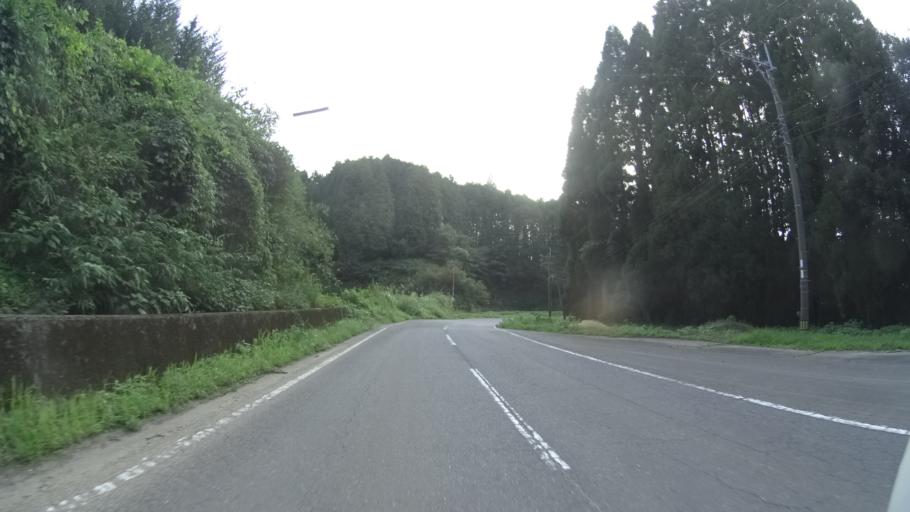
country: JP
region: Kumamoto
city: Ozu
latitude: 32.6892
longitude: 131.0126
